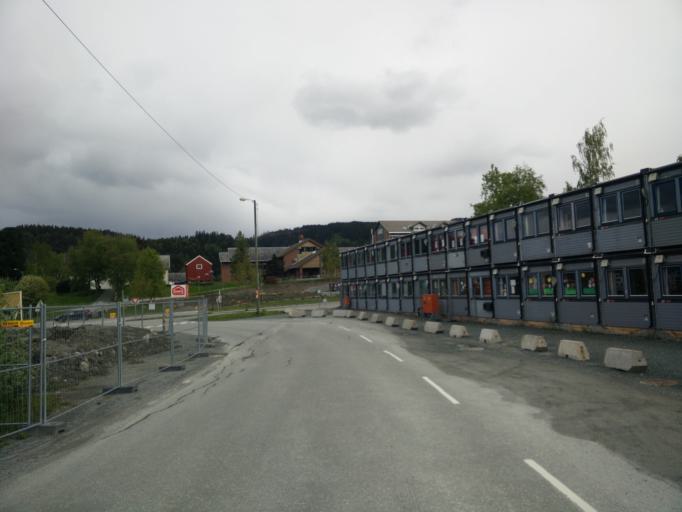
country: NO
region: Sor-Trondelag
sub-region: Skaun
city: Borsa
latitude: 63.3251
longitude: 10.0646
